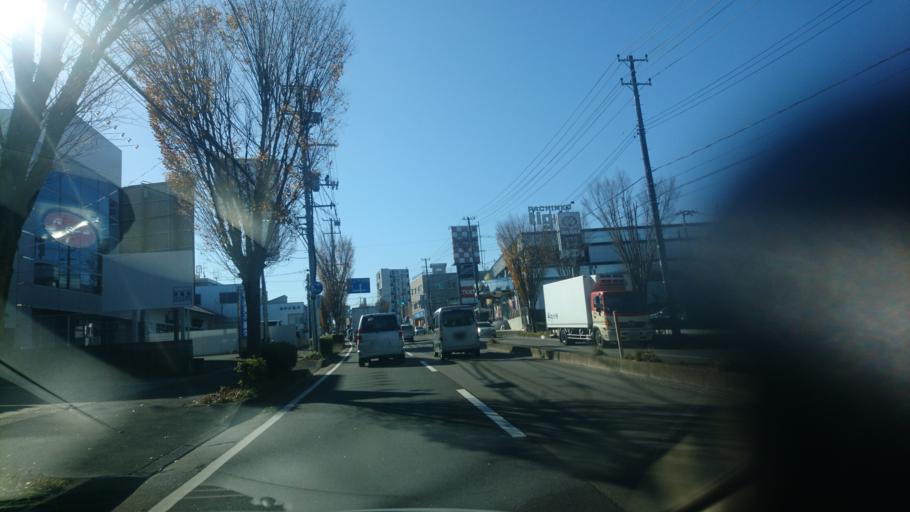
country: JP
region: Miyagi
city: Sendai-shi
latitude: 38.2918
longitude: 140.8215
